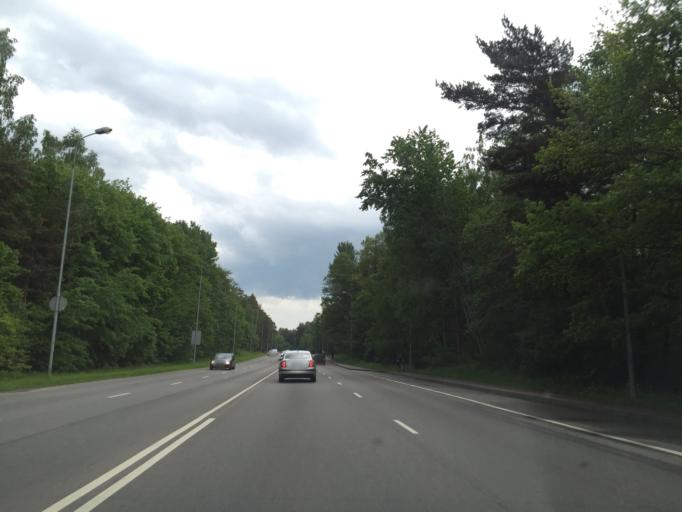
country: LT
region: Klaipedos apskritis
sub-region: Klaipeda
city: Klaipeda
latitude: 55.7370
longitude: 21.0968
